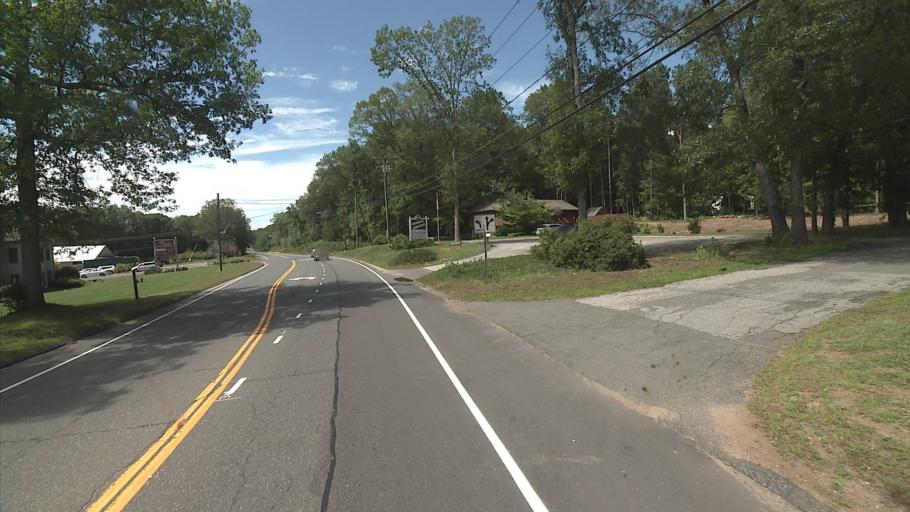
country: US
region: Connecticut
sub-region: Tolland County
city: Storrs
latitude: 41.8305
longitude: -72.2716
